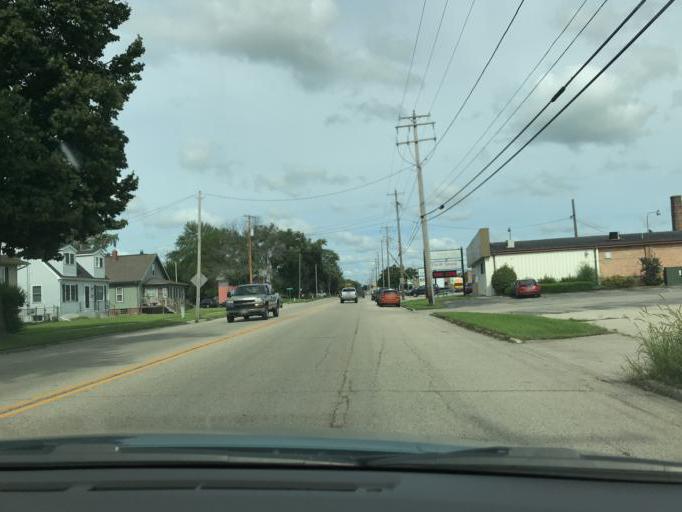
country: US
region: Wisconsin
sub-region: Racine County
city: Burlington
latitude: 42.6692
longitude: -88.2678
